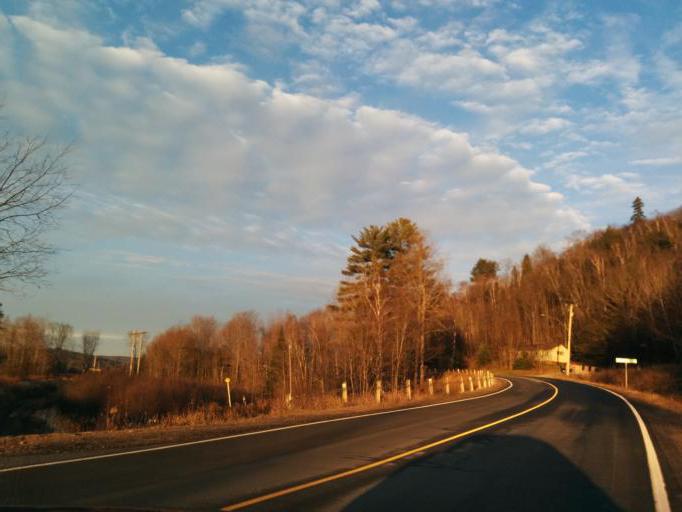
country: CA
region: Ontario
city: Bancroft
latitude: 45.0400
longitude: -78.5234
